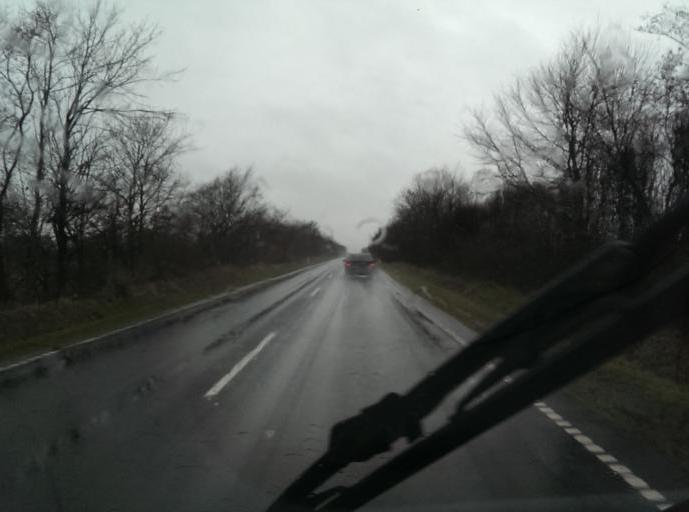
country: DK
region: South Denmark
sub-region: Varde Kommune
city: Olgod
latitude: 55.7116
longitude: 8.6092
